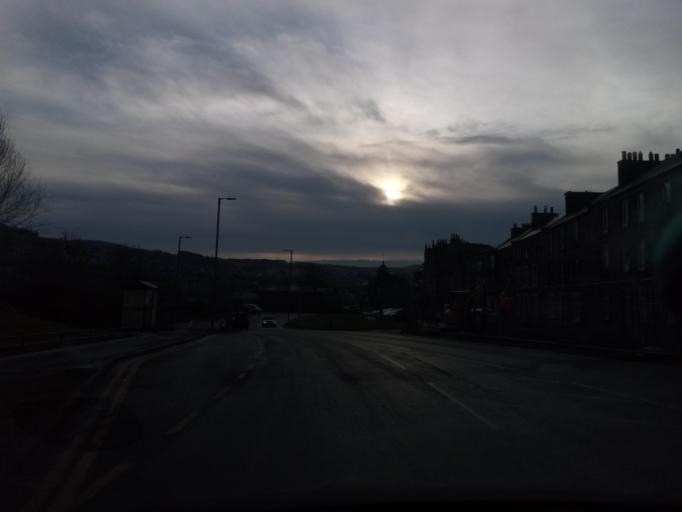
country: GB
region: Scotland
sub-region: The Scottish Borders
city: Hawick
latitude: 55.4292
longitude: -2.7853
